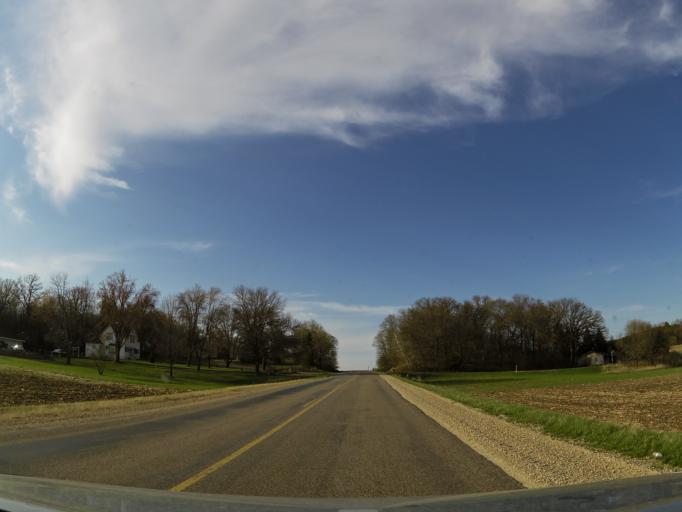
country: US
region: Wisconsin
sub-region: Pierce County
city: River Falls
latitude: 44.7543
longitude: -92.6395
